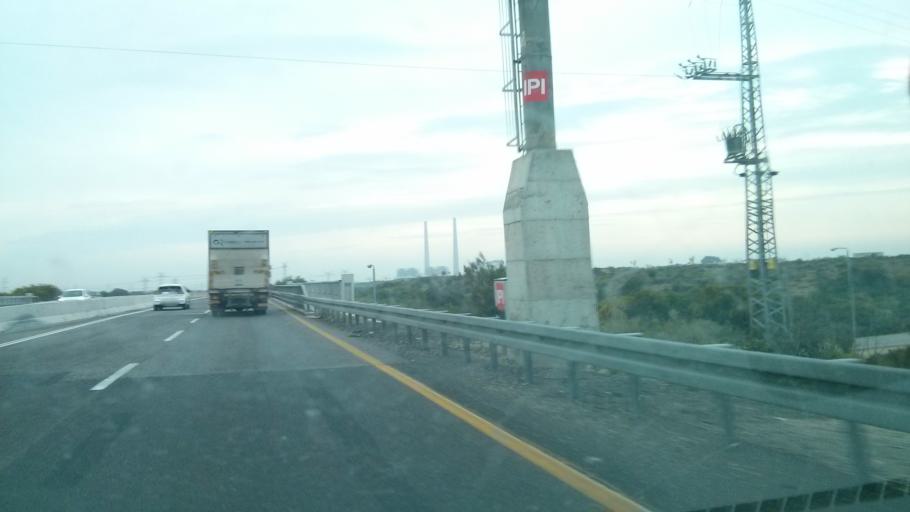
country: IL
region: Haifa
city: Qesarya
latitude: 32.4850
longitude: 34.9132
